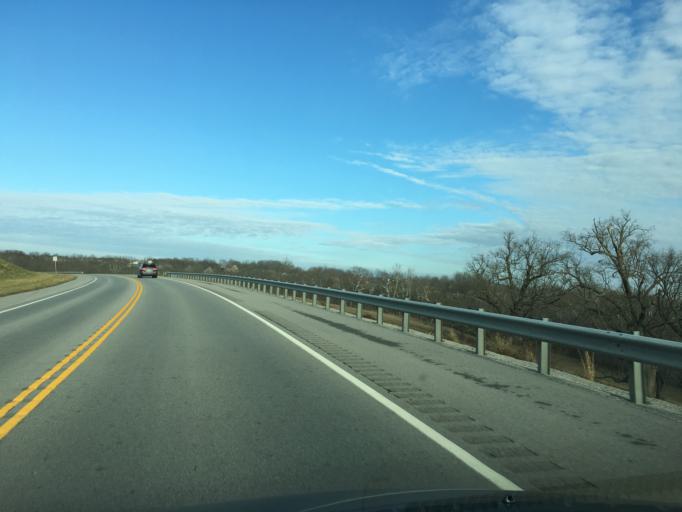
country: US
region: Kentucky
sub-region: Scott County
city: Georgetown
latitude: 38.2233
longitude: -84.5868
